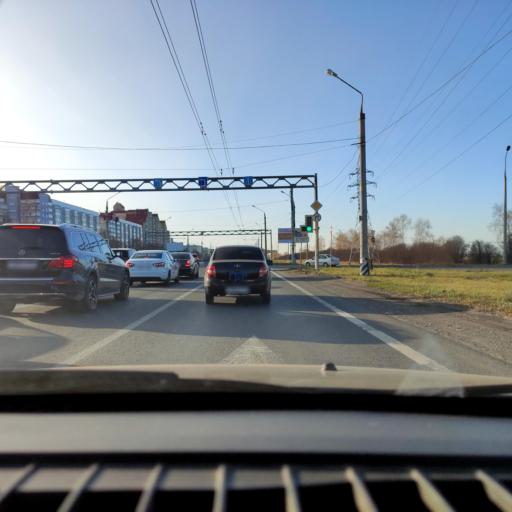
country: RU
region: Samara
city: Tol'yatti
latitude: 53.5459
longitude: 49.3735
